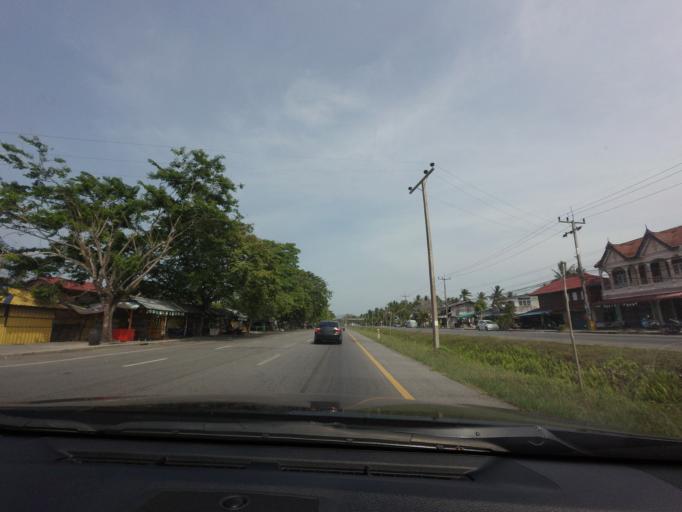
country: TH
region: Pattani
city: Yaring
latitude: 6.8184
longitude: 101.4095
